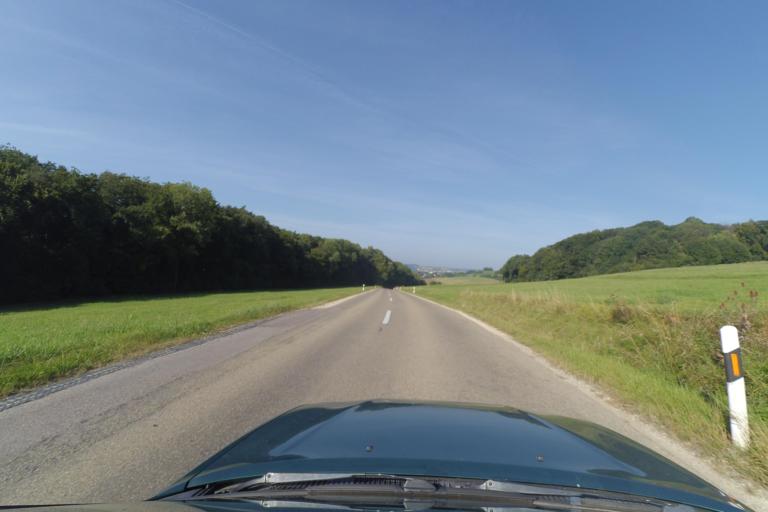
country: DE
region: Bavaria
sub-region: Swabia
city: Marxheim
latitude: 48.7424
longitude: 10.9329
